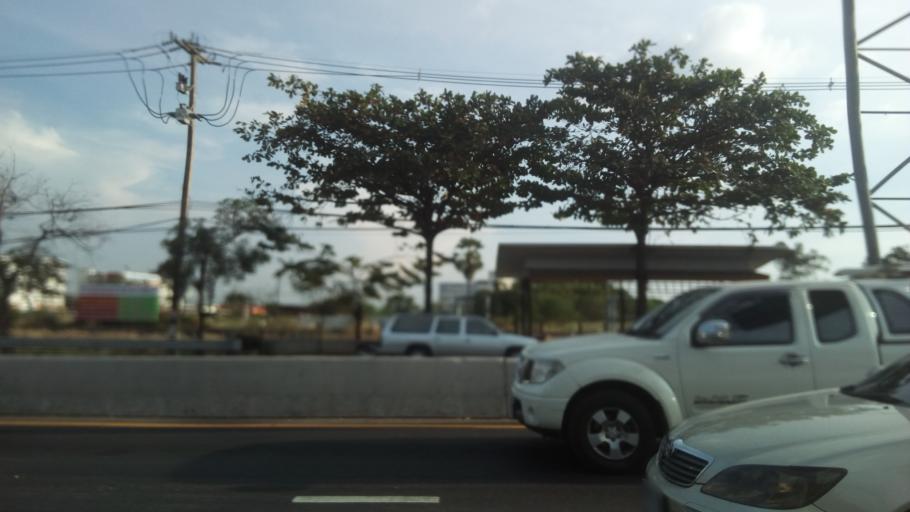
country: TH
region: Pathum Thani
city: Ban Rangsit
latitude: 14.0283
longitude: 100.7523
